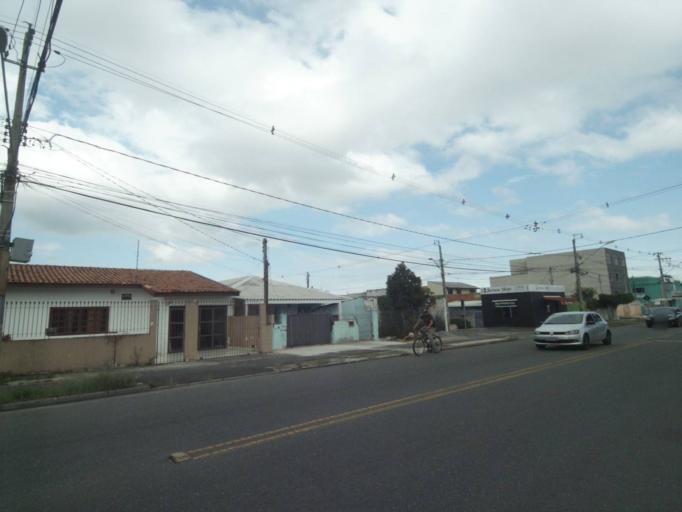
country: BR
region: Parana
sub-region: Pinhais
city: Pinhais
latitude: -25.4519
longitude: -49.2037
